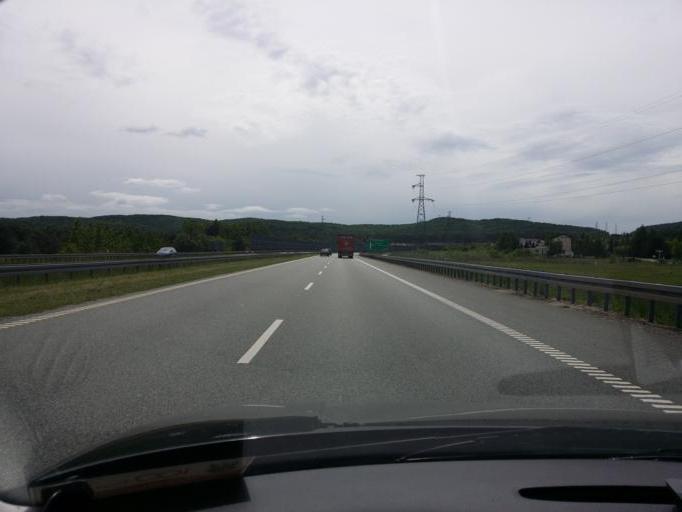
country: PL
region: Swietokrzyskie
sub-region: Powiat kielecki
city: Piekoszow
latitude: 50.8643
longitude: 20.5131
